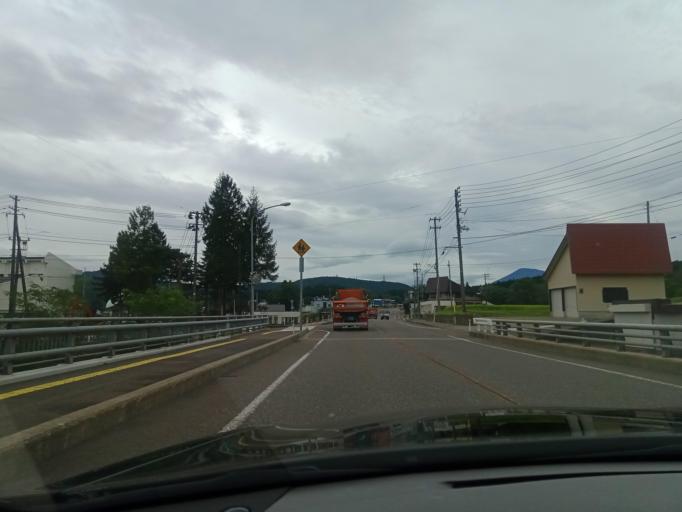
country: JP
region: Niigata
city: Arai
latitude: 36.8832
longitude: 138.2054
